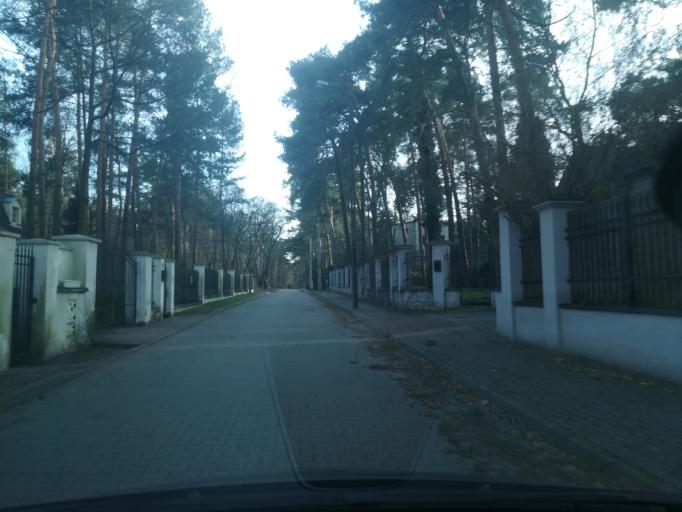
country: PL
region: Masovian Voivodeship
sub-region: Powiat piaseczynski
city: Konstancin-Jeziorna
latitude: 52.0810
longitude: 21.1067
